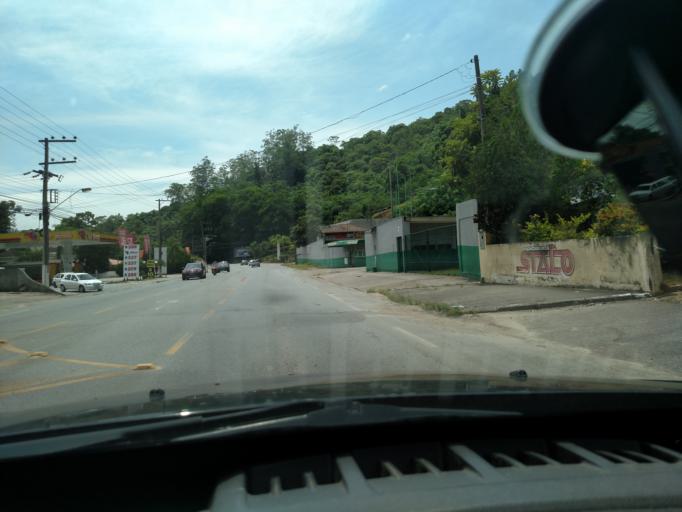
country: BR
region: Santa Catarina
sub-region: Blumenau
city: Blumenau
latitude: -26.9111
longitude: -49.0457
